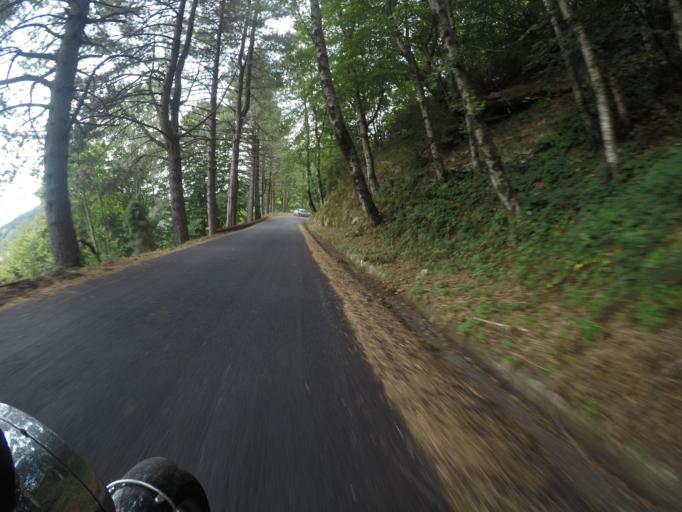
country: IT
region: Tuscany
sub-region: Provincia di Massa-Carrara
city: Carrara
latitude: 44.1198
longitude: 10.1164
